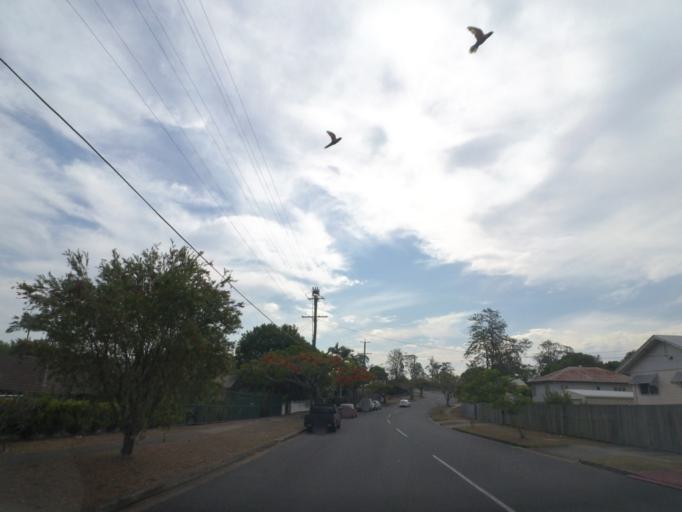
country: AU
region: Queensland
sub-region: Brisbane
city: Inala
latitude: -27.5913
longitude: 152.9640
